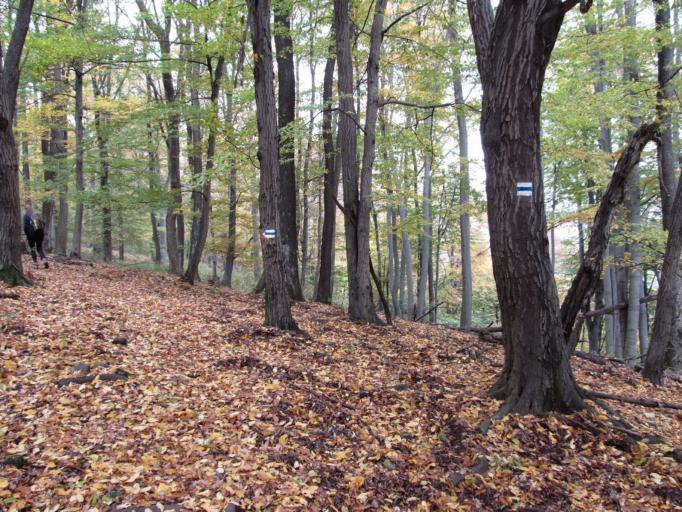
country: SK
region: Nitriansky
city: Sahy
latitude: 48.0186
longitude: 19.0010
